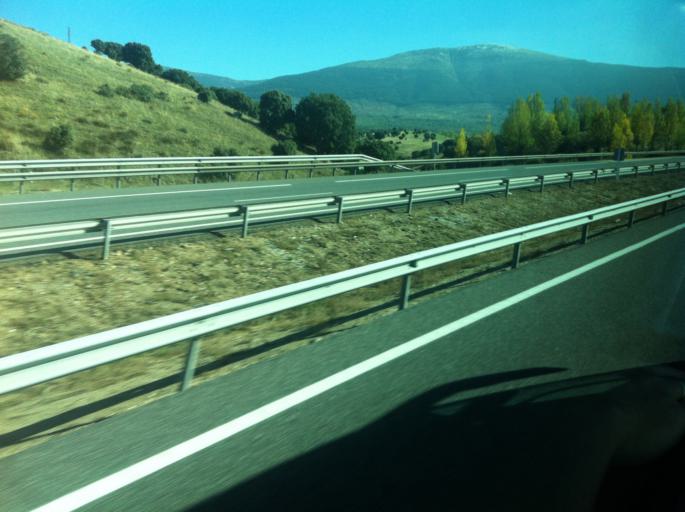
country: ES
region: Castille and Leon
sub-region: Provincia de Segovia
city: Cerezo de Abajo
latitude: 41.2118
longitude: -3.5803
